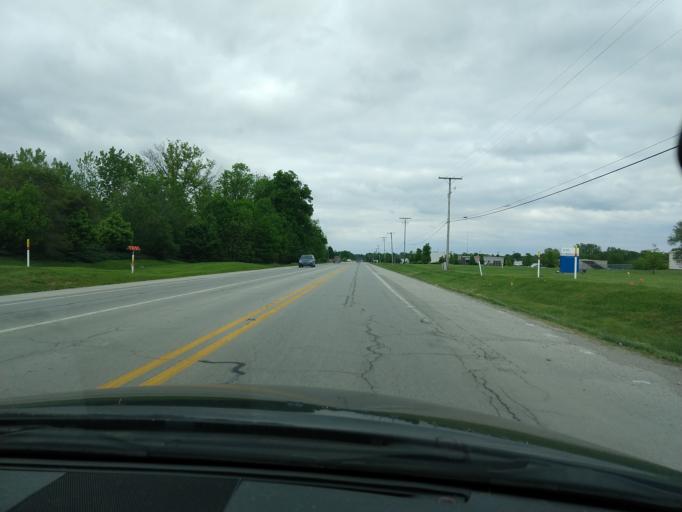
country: US
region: Indiana
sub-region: Hamilton County
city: Noblesville
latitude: 40.0432
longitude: -86.0611
